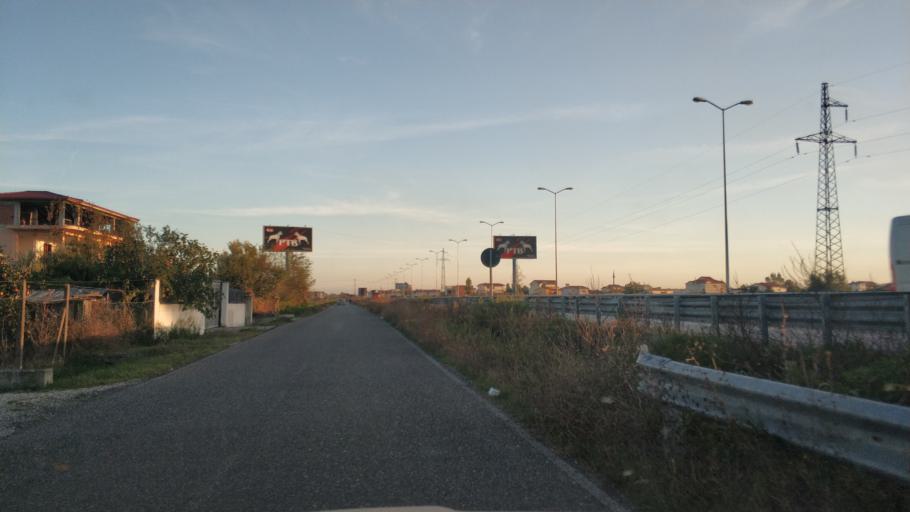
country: AL
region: Tirane
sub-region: Rrethi i Kavajes
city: Synej
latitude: 41.1877
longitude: 19.5422
